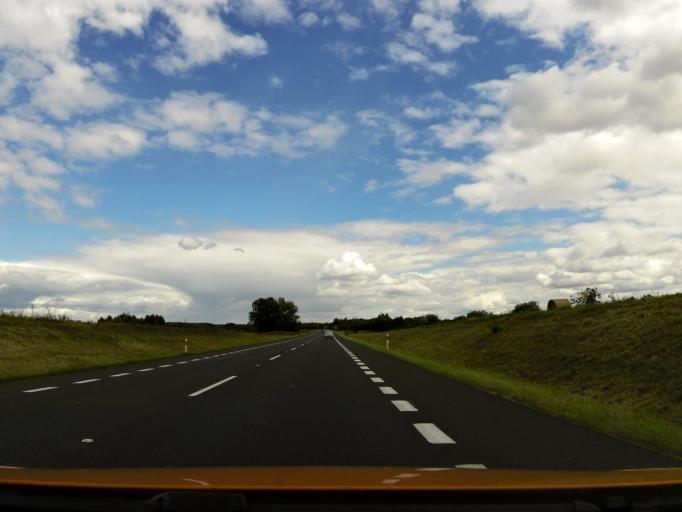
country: PL
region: West Pomeranian Voivodeship
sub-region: Powiat goleniowski
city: Goleniow
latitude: 53.5884
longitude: 14.8539
